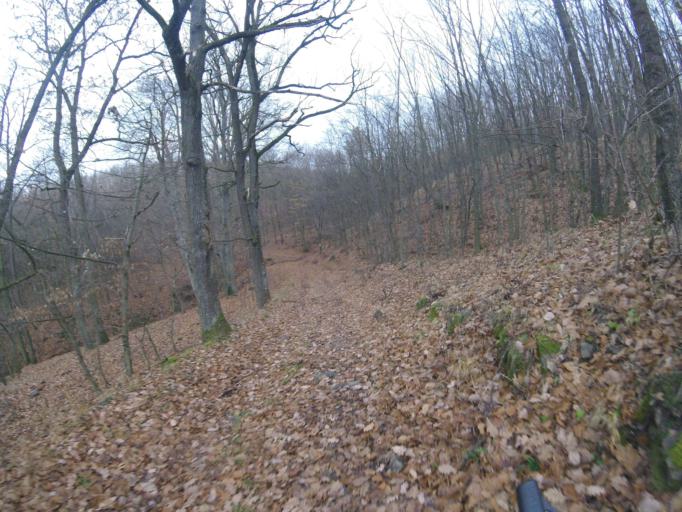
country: HU
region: Pest
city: Szob
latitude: 47.8791
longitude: 18.8370
